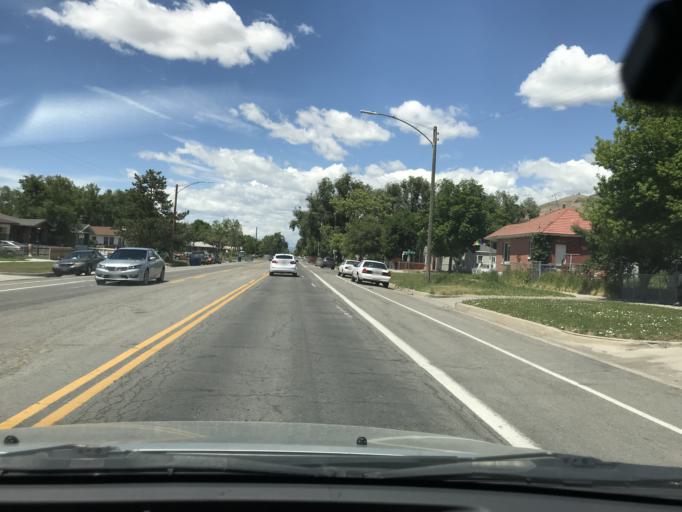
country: US
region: Utah
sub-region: Salt Lake County
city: Salt Lake City
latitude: 40.7764
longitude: -111.9168
